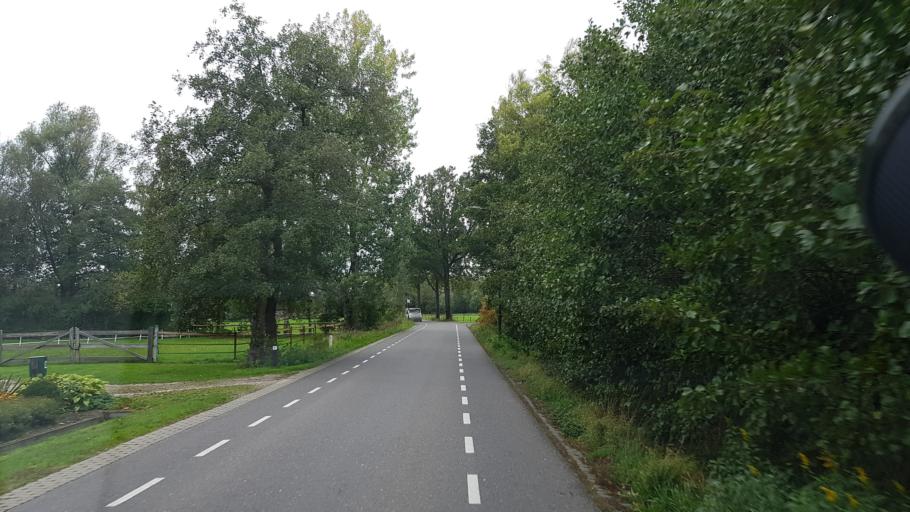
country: NL
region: Gelderland
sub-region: Gemeente Apeldoorn
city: Loenen
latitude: 52.1750
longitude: 6.0224
